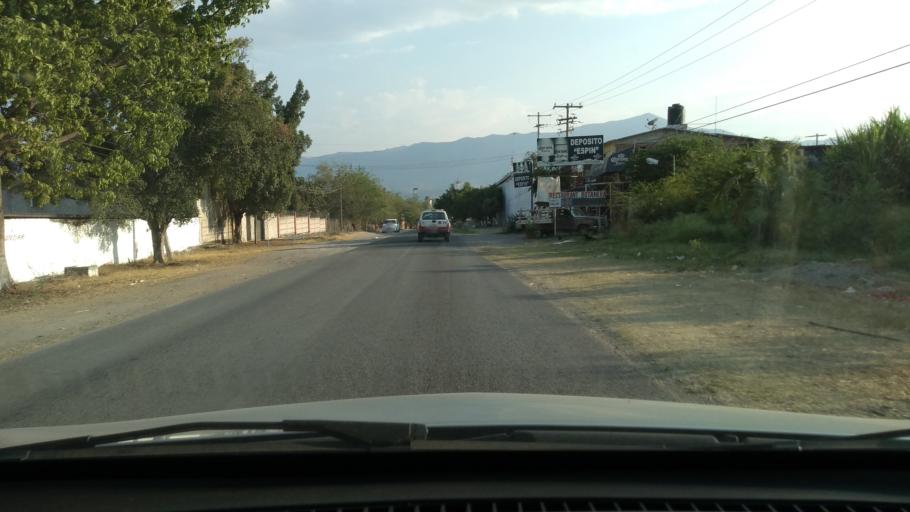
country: MX
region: Morelos
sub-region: Jojutla
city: Tehuixtla
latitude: 18.5660
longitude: -99.2694
